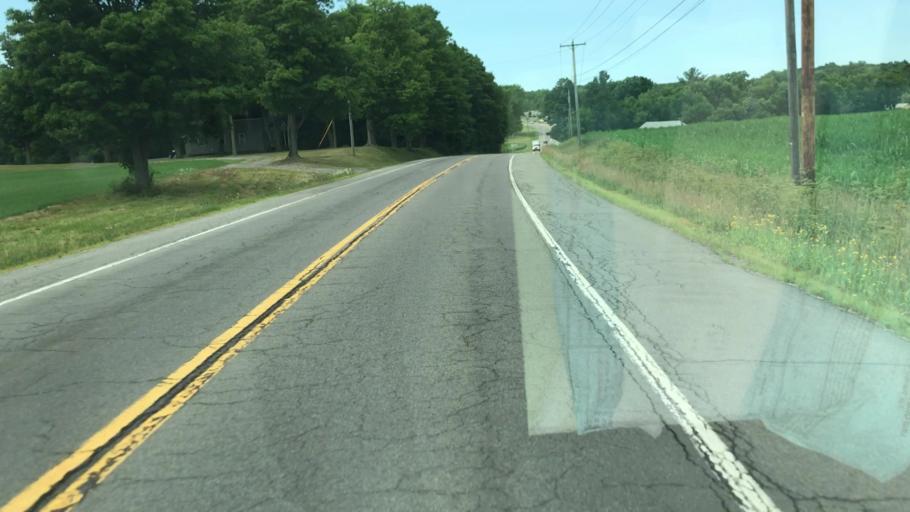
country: US
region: New York
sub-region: Onondaga County
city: Skaneateles
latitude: 42.9421
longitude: -76.3859
